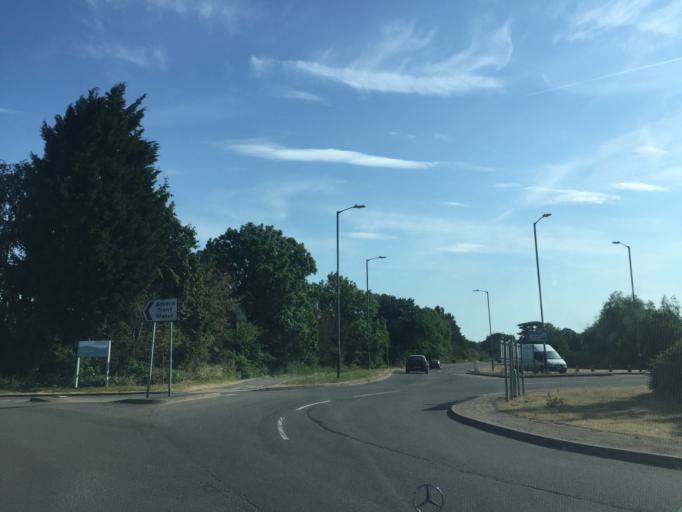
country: GB
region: England
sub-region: Warwickshire
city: Warwick
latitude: 52.2641
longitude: -1.6031
